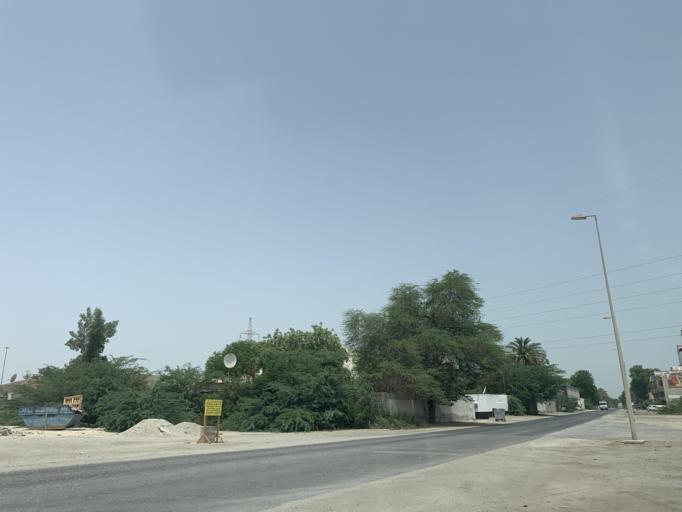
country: BH
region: Northern
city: Ar Rifa'
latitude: 26.1263
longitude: 50.5930
